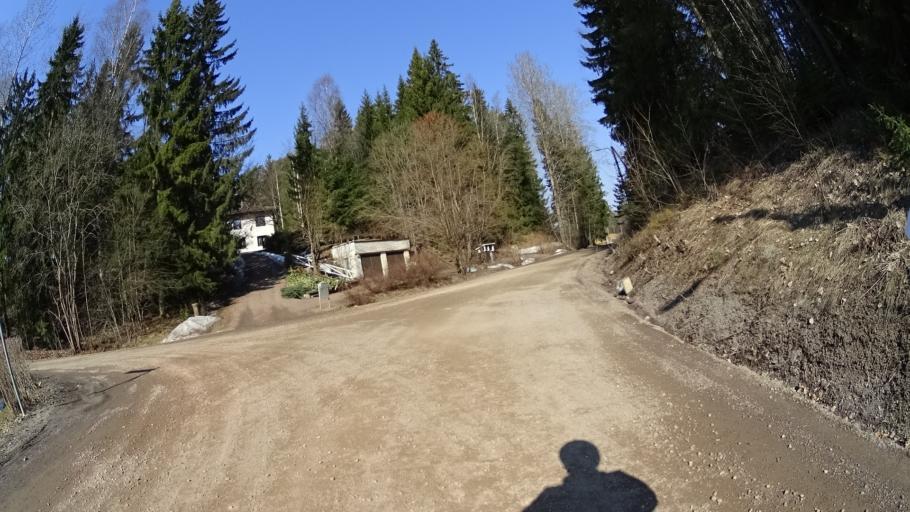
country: FI
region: Uusimaa
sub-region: Helsinki
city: Espoo
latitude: 60.2348
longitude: 24.5963
